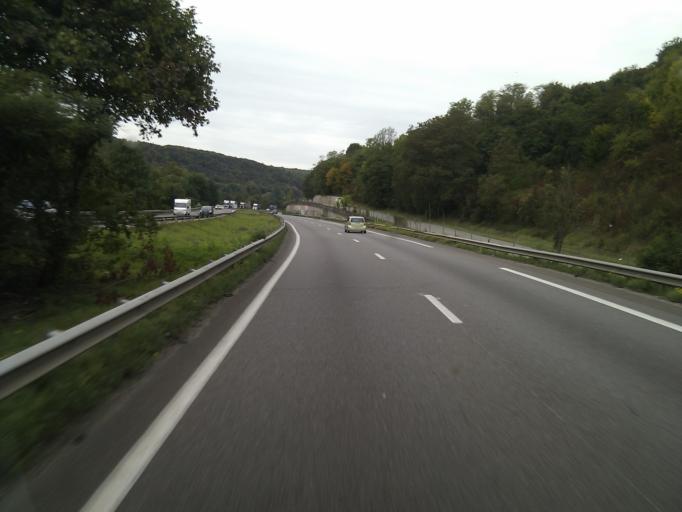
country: FR
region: Lorraine
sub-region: Departement de Meurthe-et-Moselle
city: Custines
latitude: 48.7921
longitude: 6.1330
